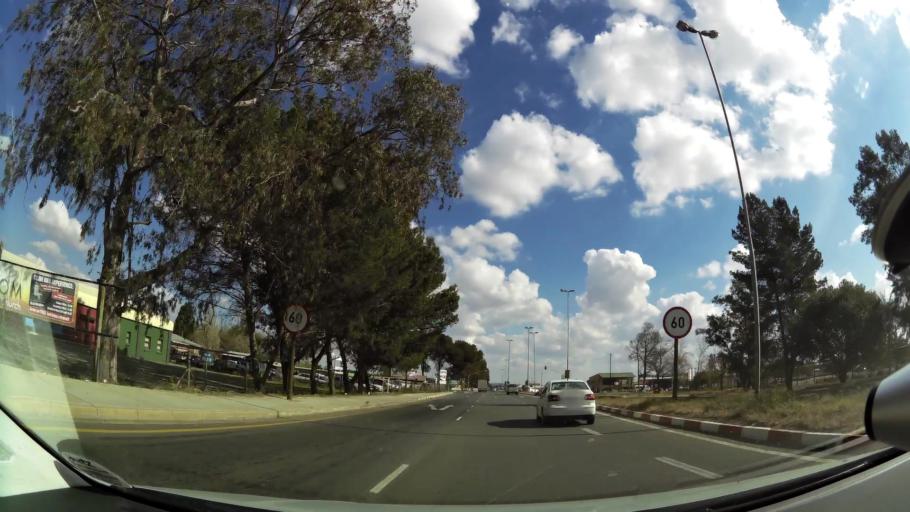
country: ZA
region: Orange Free State
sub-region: Mangaung Metropolitan Municipality
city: Bloemfontein
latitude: -29.1279
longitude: 26.1573
